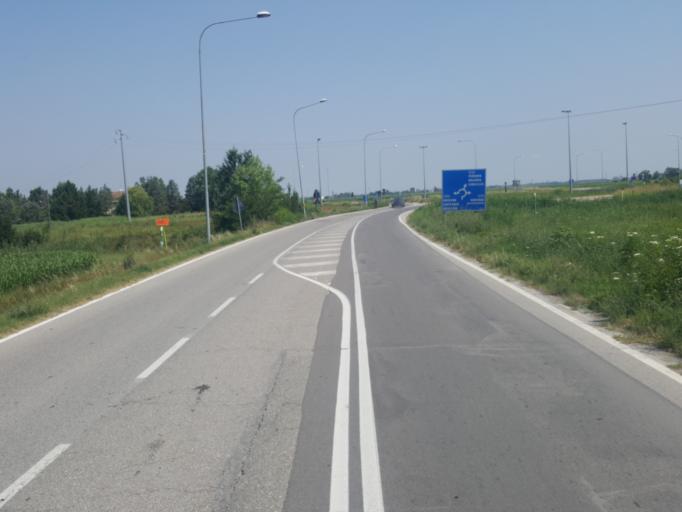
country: IT
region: Emilia-Romagna
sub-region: Provincia di Ravenna
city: Massa Lombarda
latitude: 44.4549
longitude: 11.7940
